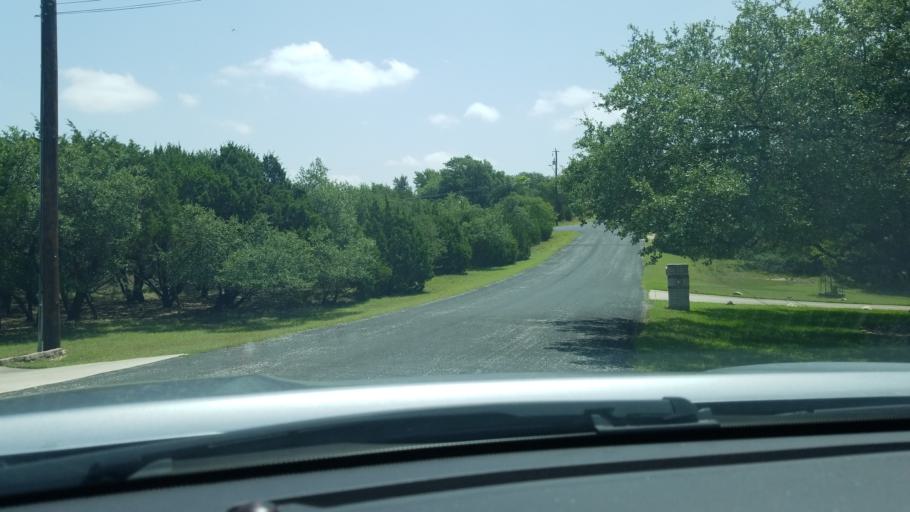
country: US
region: Texas
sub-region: Bexar County
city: Timberwood Park
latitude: 29.6941
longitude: -98.4882
